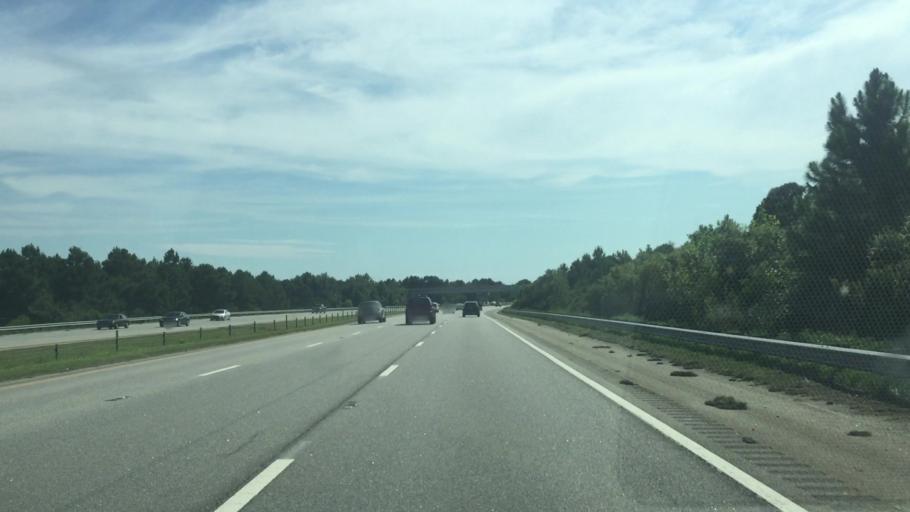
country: US
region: South Carolina
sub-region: Horry County
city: North Myrtle Beach
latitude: 33.8202
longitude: -78.7381
